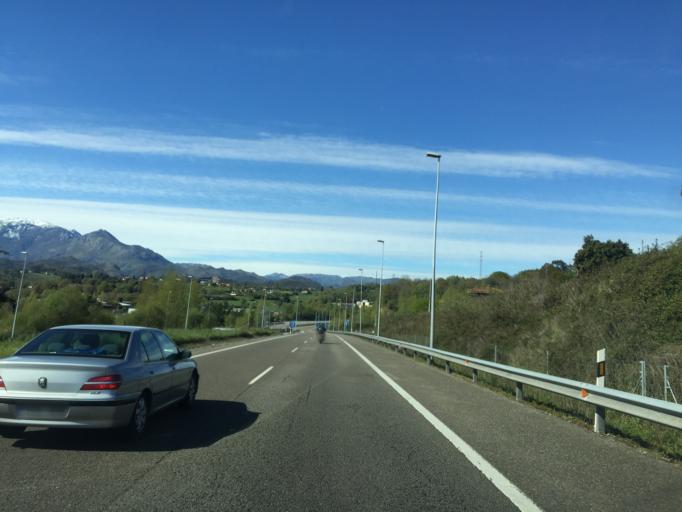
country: ES
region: Asturias
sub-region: Province of Asturias
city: Oviedo
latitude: 43.3459
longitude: -5.8645
